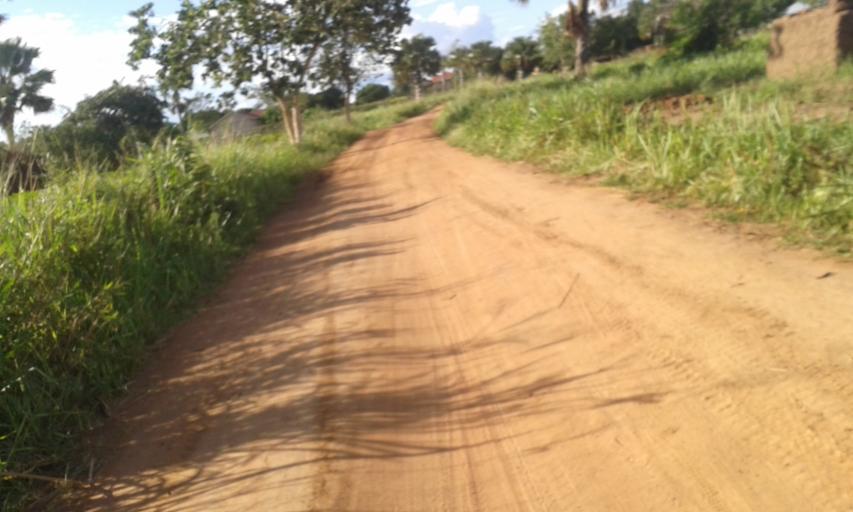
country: UG
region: Northern Region
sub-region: Gulu District
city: Gulu
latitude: 2.8037
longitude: 32.3059
